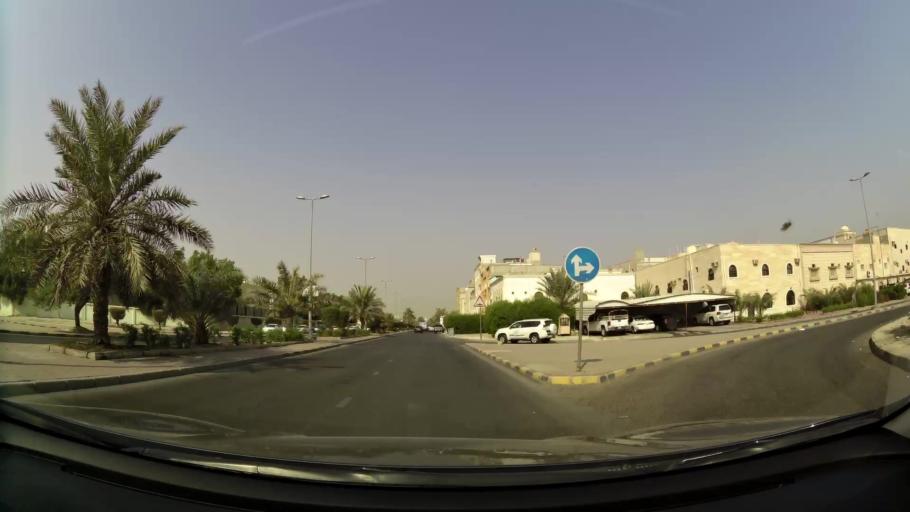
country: KW
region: Al Asimah
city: Ar Rabiyah
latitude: 29.2815
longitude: 47.8783
